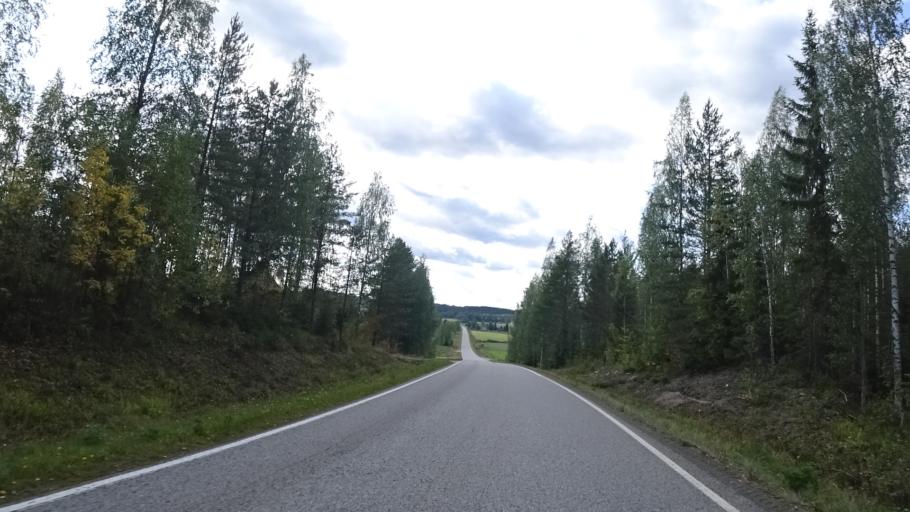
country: RU
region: Republic of Karelia
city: Vyartsilya
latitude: 62.2225
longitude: 30.6369
